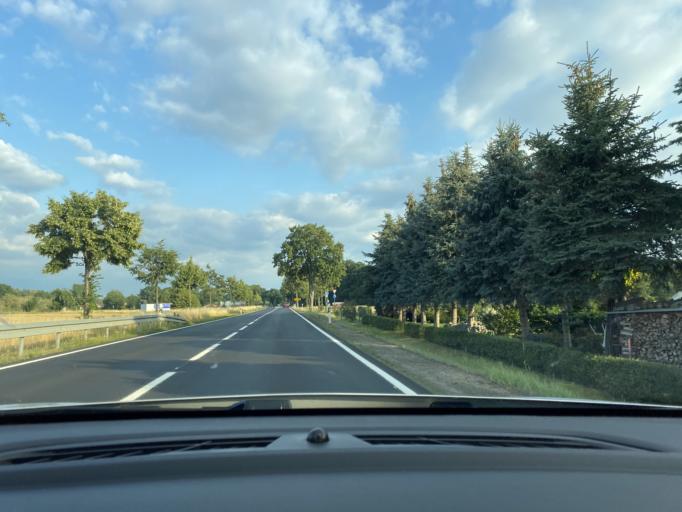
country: DE
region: Saxony
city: Neschwitz
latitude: 51.2740
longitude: 14.3409
